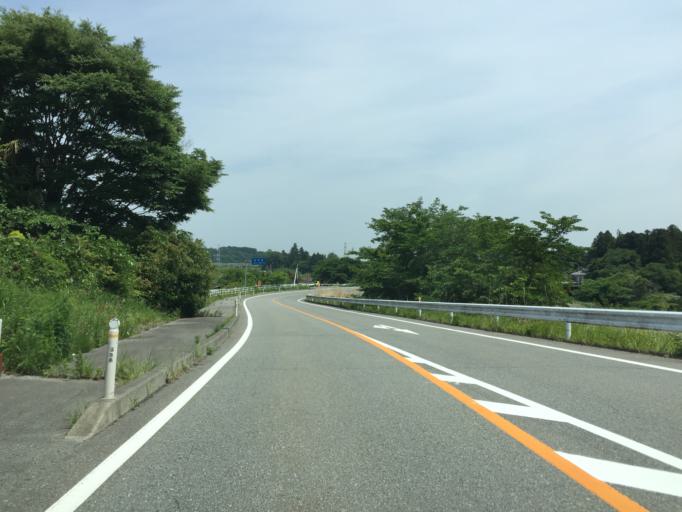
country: JP
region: Fukushima
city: Namie
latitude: 37.5084
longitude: 140.9311
